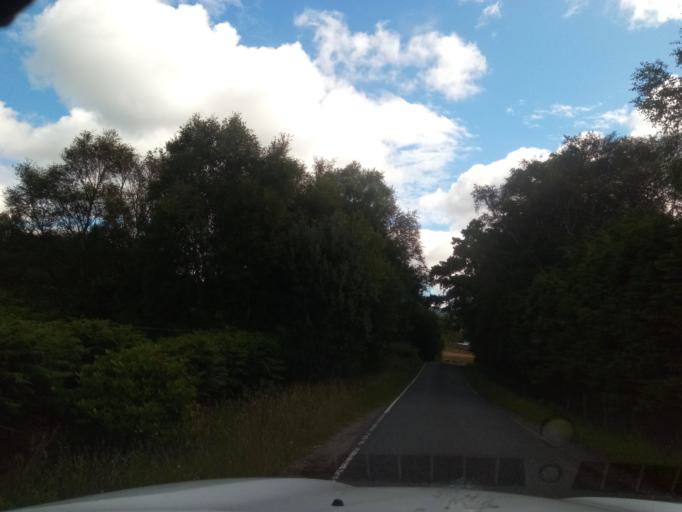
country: GB
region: Scotland
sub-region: Argyll and Bute
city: Isle Of Mull
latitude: 56.7613
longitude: -5.7612
